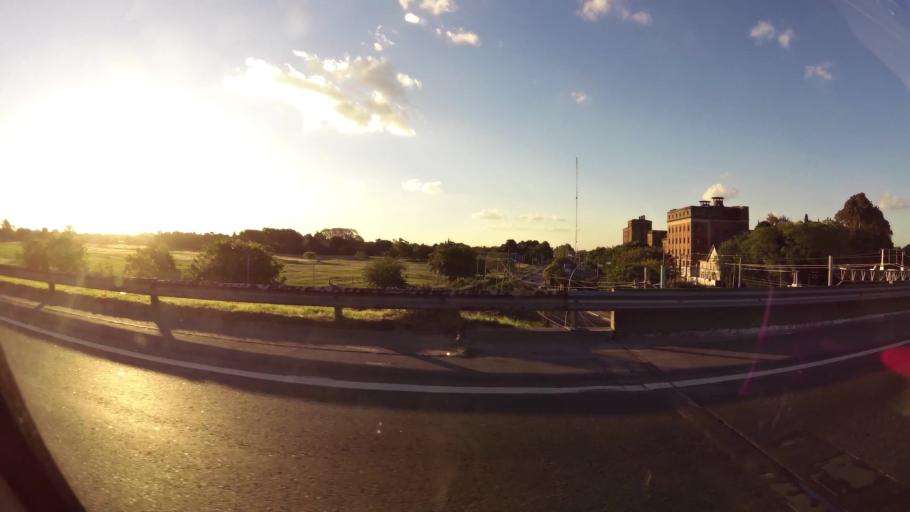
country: AR
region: Buenos Aires
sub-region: Partido de Quilmes
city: Quilmes
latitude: -34.7907
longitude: -58.1572
